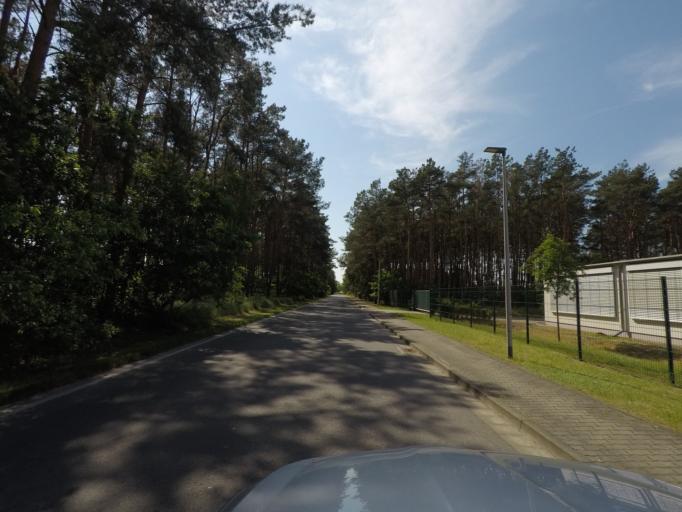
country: DE
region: Brandenburg
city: Eberswalde
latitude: 52.8539
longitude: 13.7703
